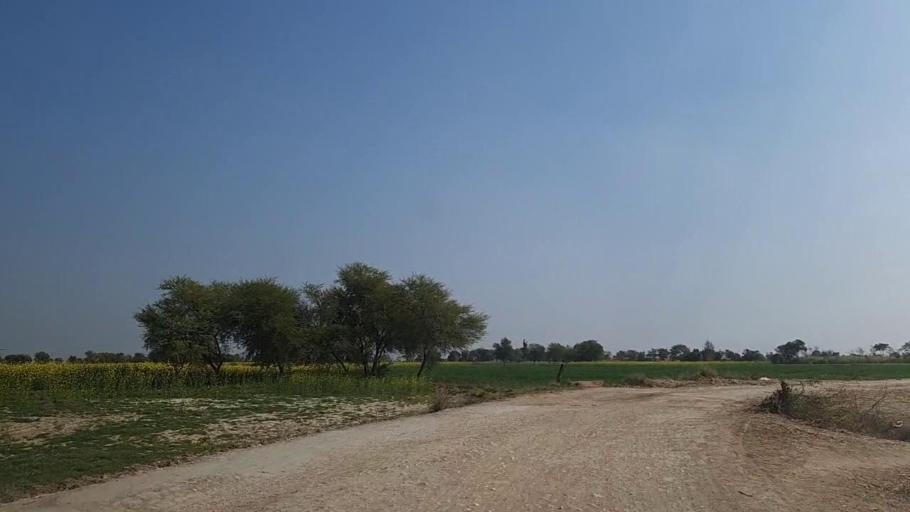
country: PK
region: Sindh
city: Daur
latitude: 26.4770
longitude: 68.2506
